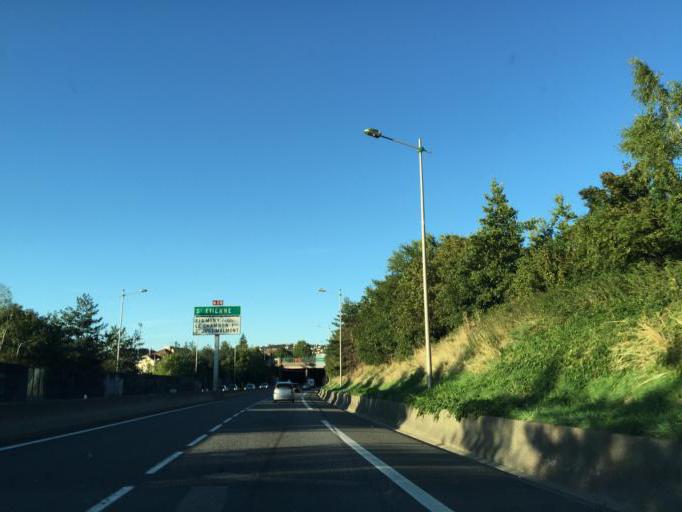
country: FR
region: Rhone-Alpes
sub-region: Departement de la Loire
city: Unieux
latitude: 45.3860
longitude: 4.2755
